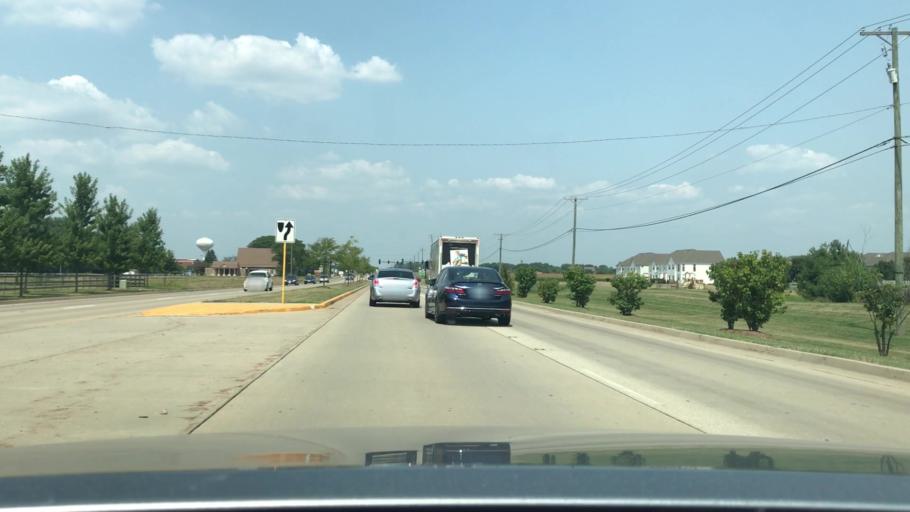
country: US
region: Illinois
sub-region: Will County
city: Plainfield
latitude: 41.5837
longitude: -88.2011
